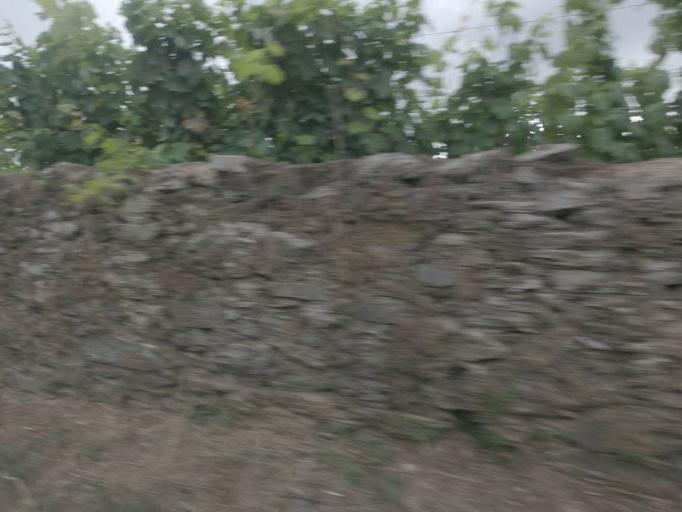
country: PT
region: Vila Real
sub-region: Sabrosa
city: Sabrosa
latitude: 41.2550
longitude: -7.5030
